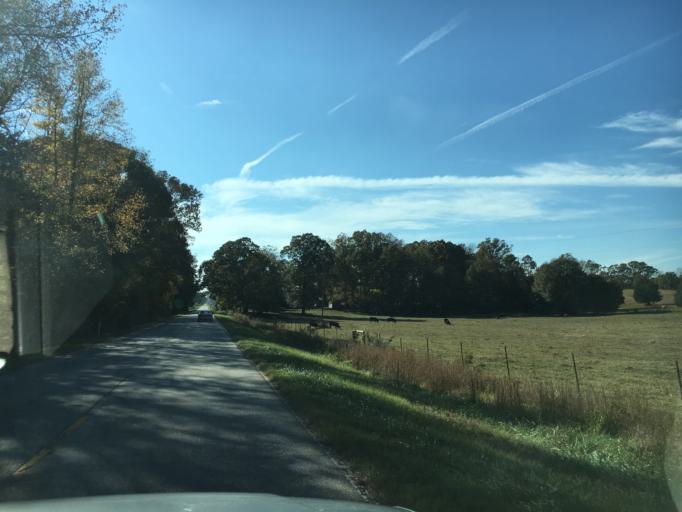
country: US
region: South Carolina
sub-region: Anderson County
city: Iva
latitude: 34.3494
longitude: -82.7367
